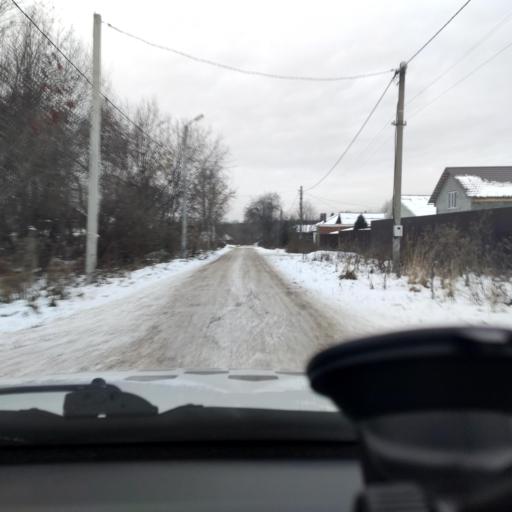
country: RU
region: Perm
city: Froly
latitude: 57.9550
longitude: 56.2891
